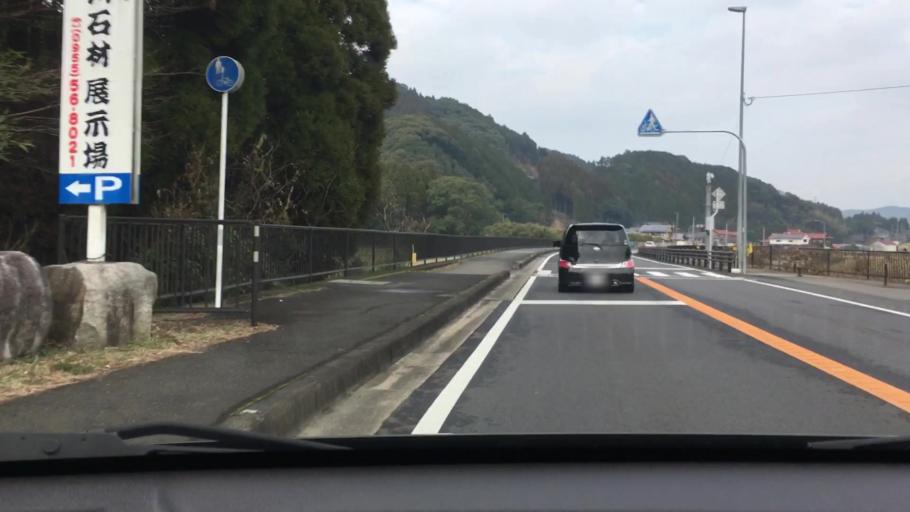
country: JP
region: Saga Prefecture
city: Imaricho-ko
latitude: 33.3227
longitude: 129.9291
